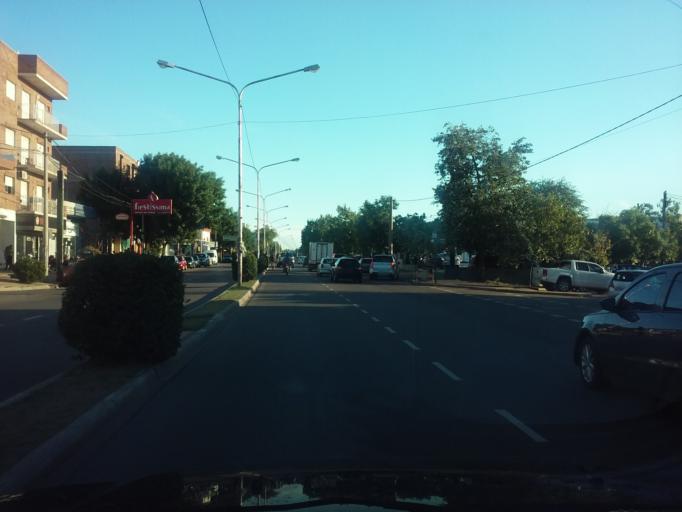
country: AR
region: La Pampa
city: Santa Rosa
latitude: -36.6263
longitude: -64.2815
